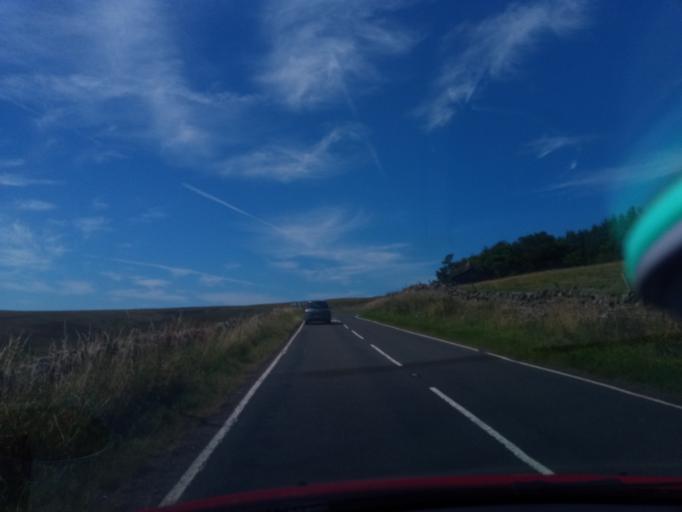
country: GB
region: England
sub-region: Northumberland
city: Bardon Mill
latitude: 54.8643
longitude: -2.3698
